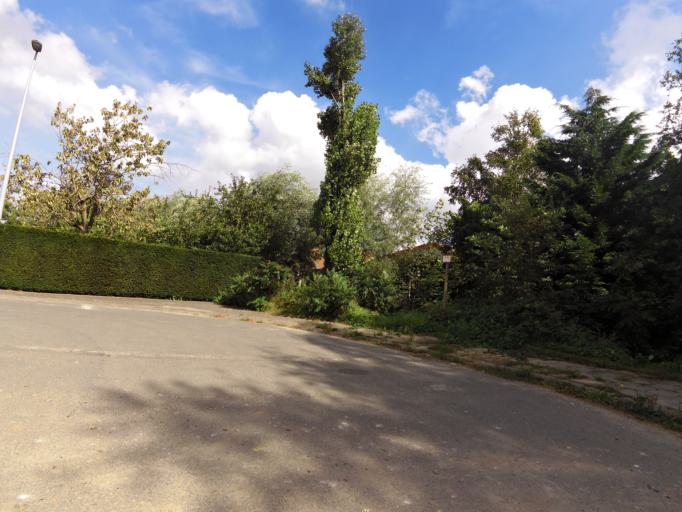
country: BE
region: Flanders
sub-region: Provincie West-Vlaanderen
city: Sint-Kruis
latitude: 51.2401
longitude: 3.2522
